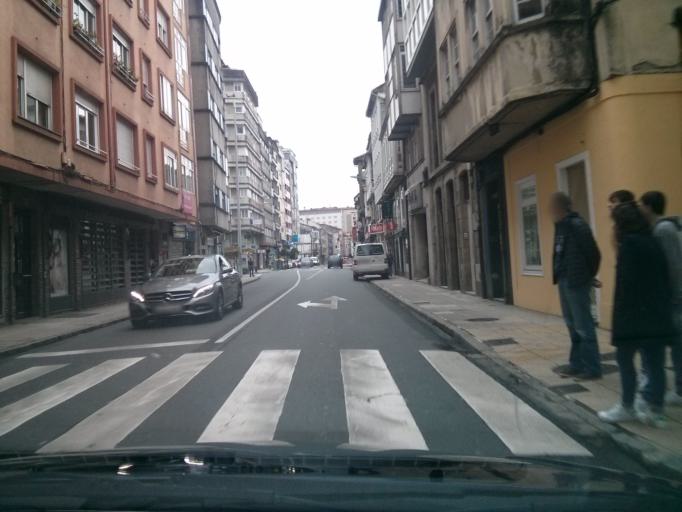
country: ES
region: Galicia
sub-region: Provincia da Coruna
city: Santiago de Compostela
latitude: 42.8742
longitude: -8.5520
